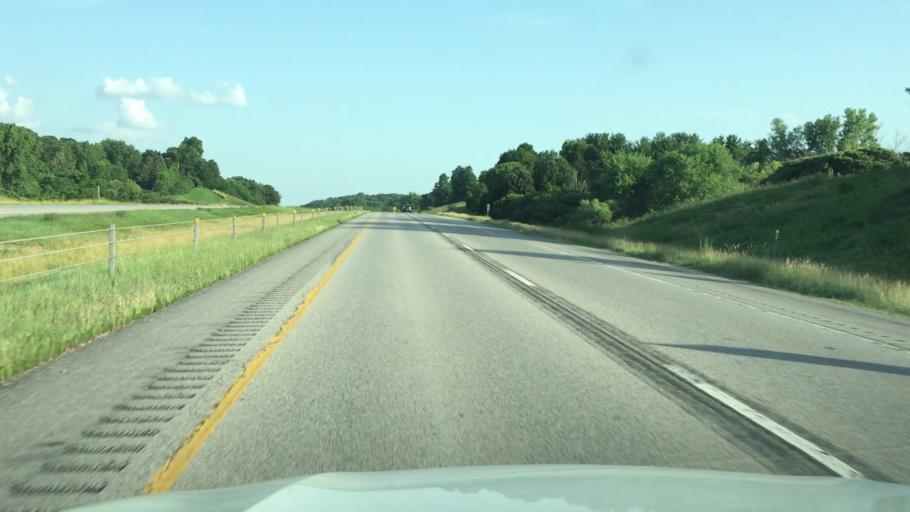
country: US
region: Iowa
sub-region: Linn County
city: Ely
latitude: 41.8365
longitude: -91.6637
